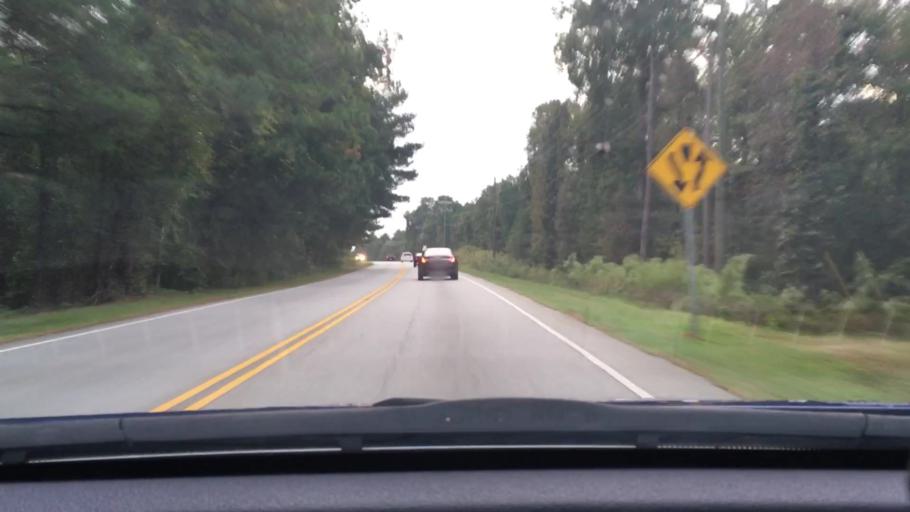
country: US
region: South Carolina
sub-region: Lexington County
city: Irmo
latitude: 34.0885
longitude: -81.1487
